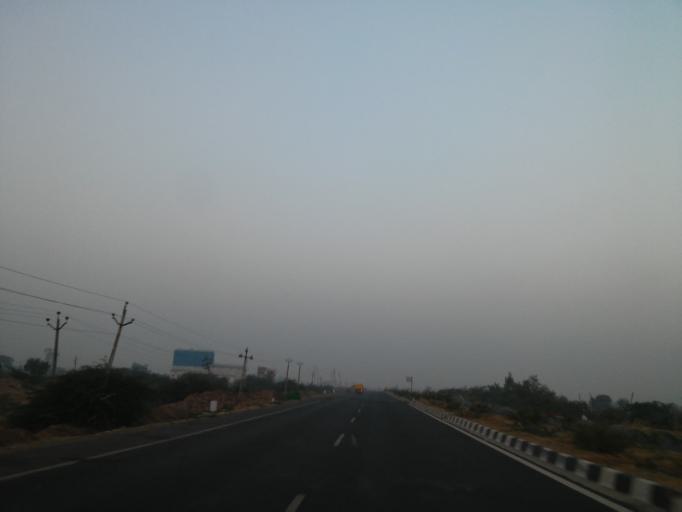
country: IN
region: Gujarat
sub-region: Surendranagar
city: Dhrangadhra
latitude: 23.0006
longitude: 71.3653
